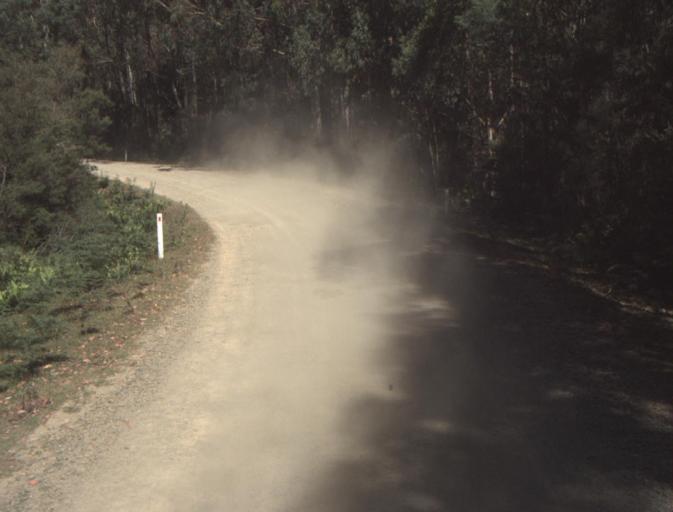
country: AU
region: Tasmania
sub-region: Dorset
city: Scottsdale
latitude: -41.3855
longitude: 147.5025
